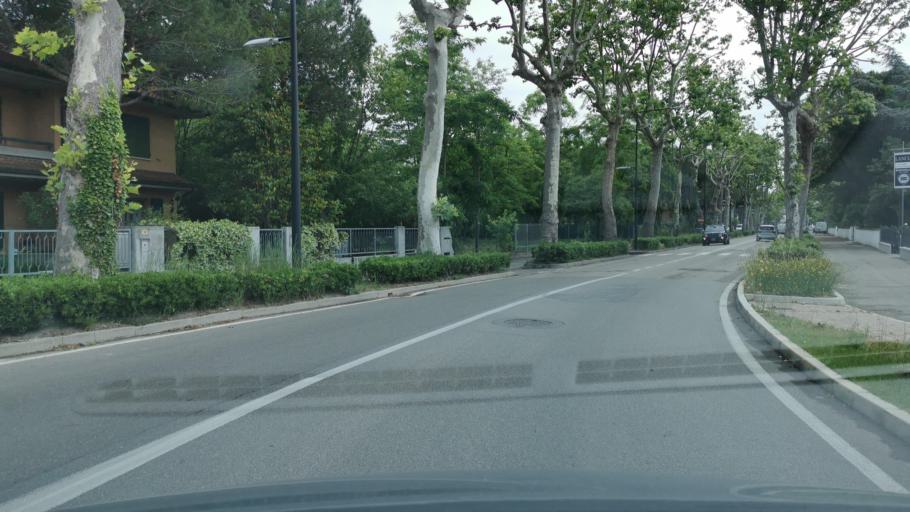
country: IT
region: Emilia-Romagna
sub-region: Provincia di Ravenna
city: Cervia
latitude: 44.2663
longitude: 12.3408
